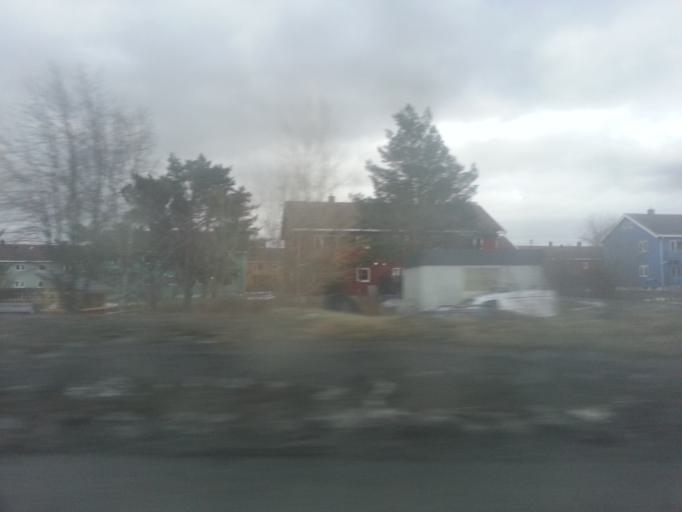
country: NO
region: Sor-Trondelag
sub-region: Trondheim
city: Trondheim
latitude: 63.4308
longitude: 10.4549
